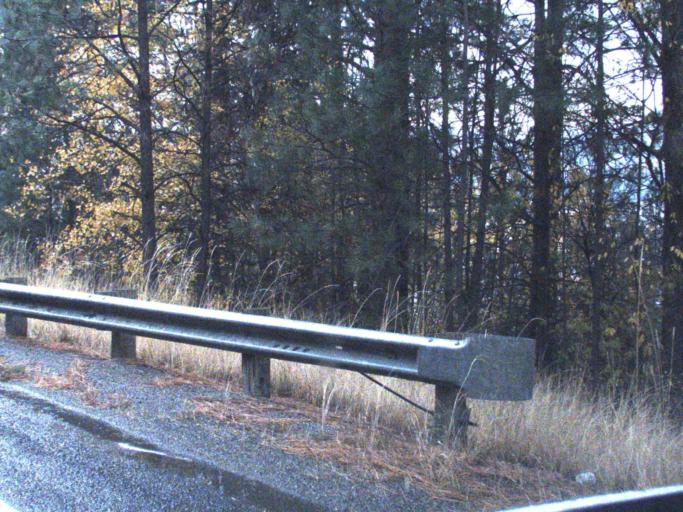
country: US
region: Washington
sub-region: Stevens County
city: Kettle Falls
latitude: 48.5214
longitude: -118.1398
